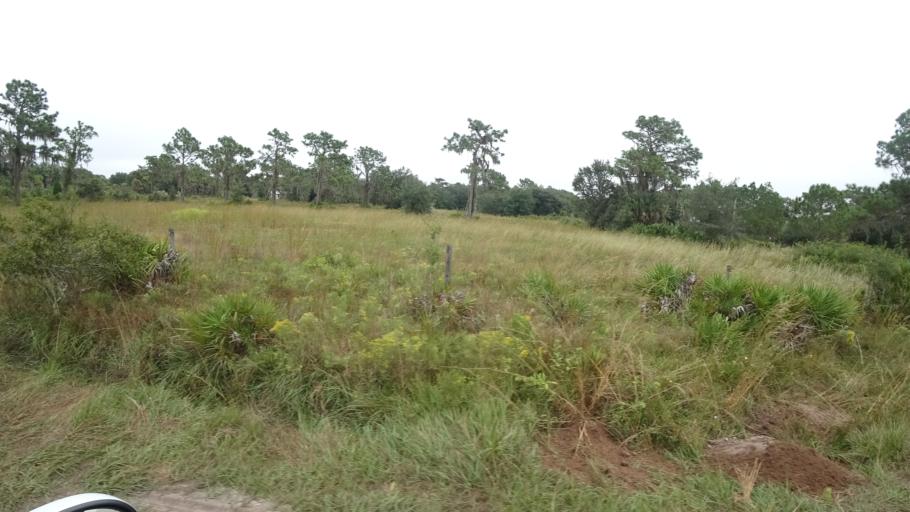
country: US
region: Florida
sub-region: Sarasota County
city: Warm Mineral Springs
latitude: 27.2746
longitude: -82.1253
